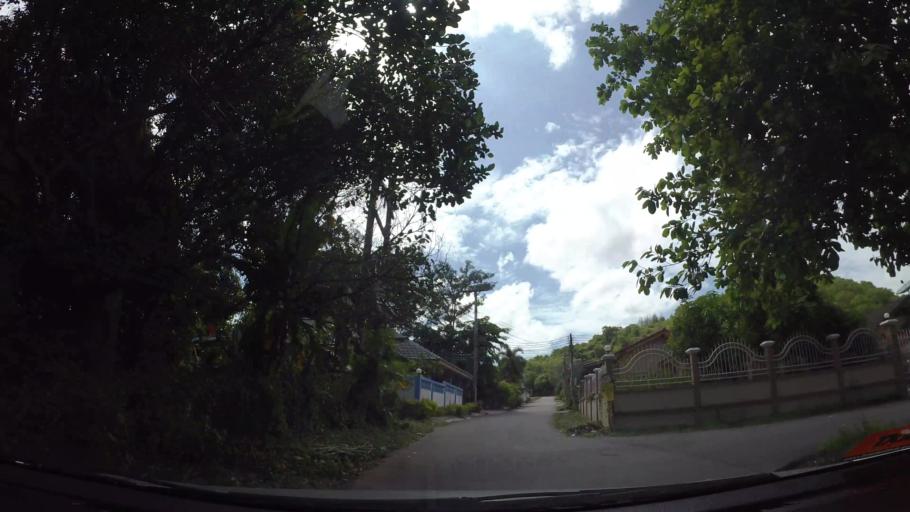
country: TH
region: Chon Buri
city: Sattahip
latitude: 12.6923
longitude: 100.9055
